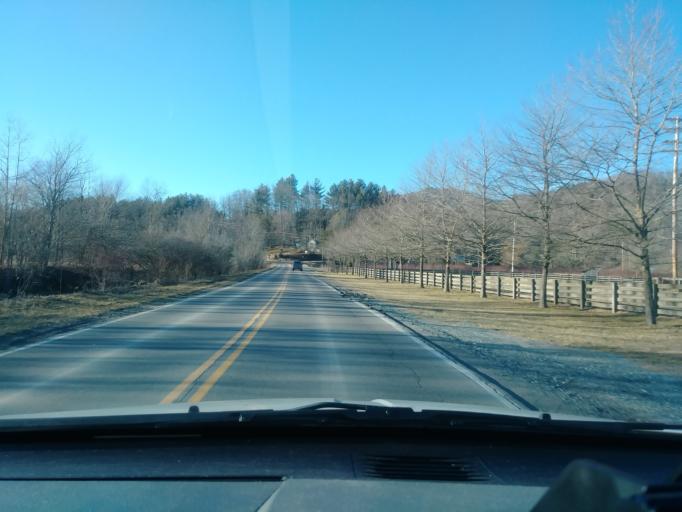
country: US
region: North Carolina
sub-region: Avery County
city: Banner Elk
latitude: 36.1515
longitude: -81.8616
